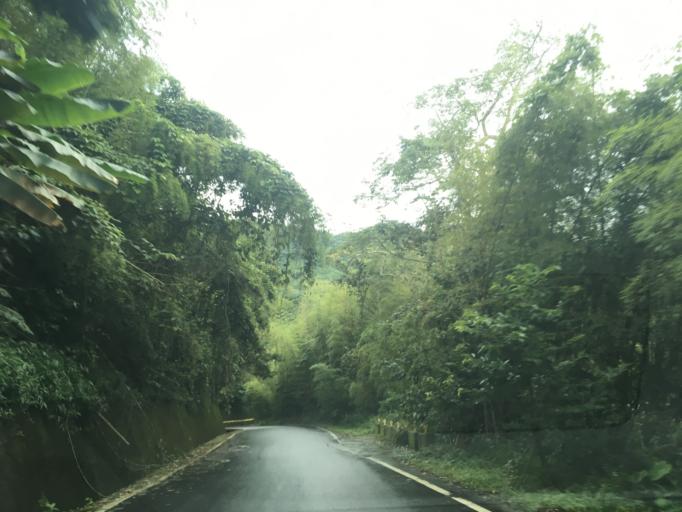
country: TW
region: Taiwan
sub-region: Chiayi
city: Jiayi Shi
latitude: 23.4460
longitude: 120.6671
